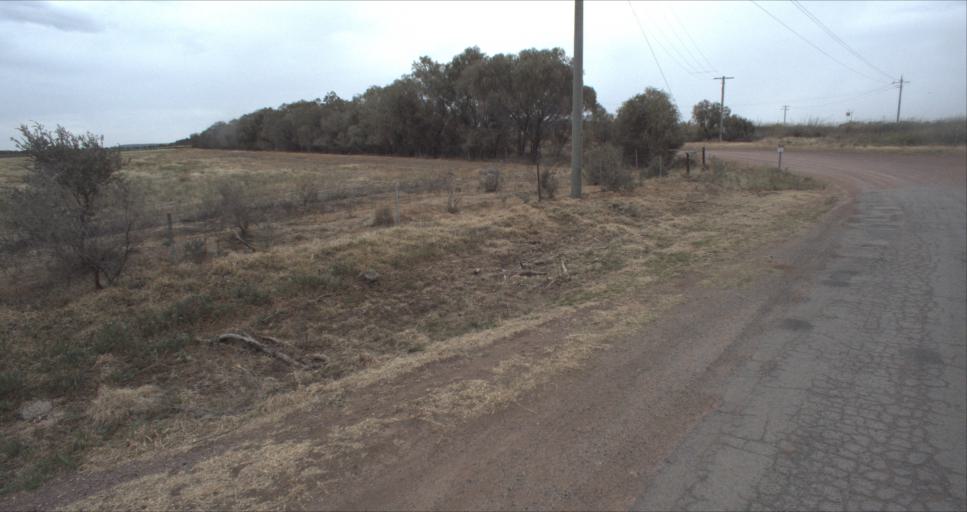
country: AU
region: New South Wales
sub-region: Leeton
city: Leeton
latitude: -34.4042
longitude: 146.3416
